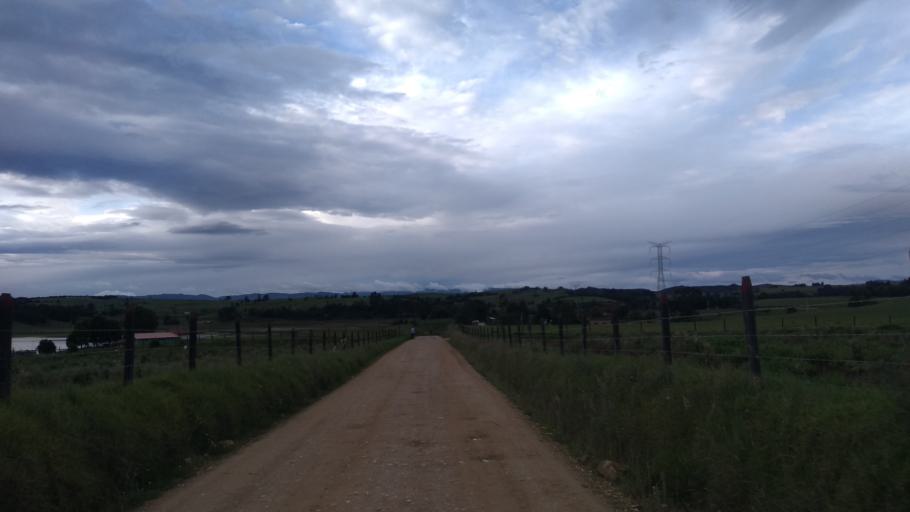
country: CO
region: Boyaca
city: Toca
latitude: 5.6113
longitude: -73.1748
